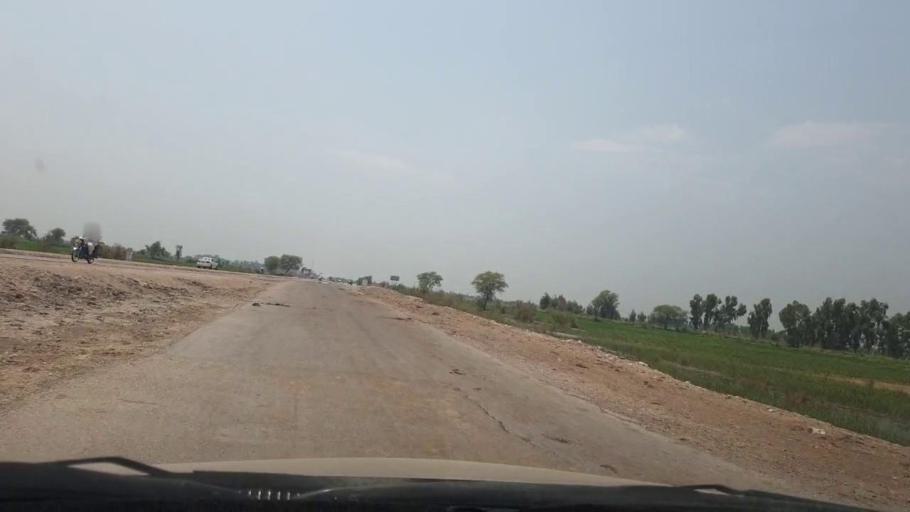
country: PK
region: Sindh
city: Ratodero
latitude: 27.7146
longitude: 68.2768
